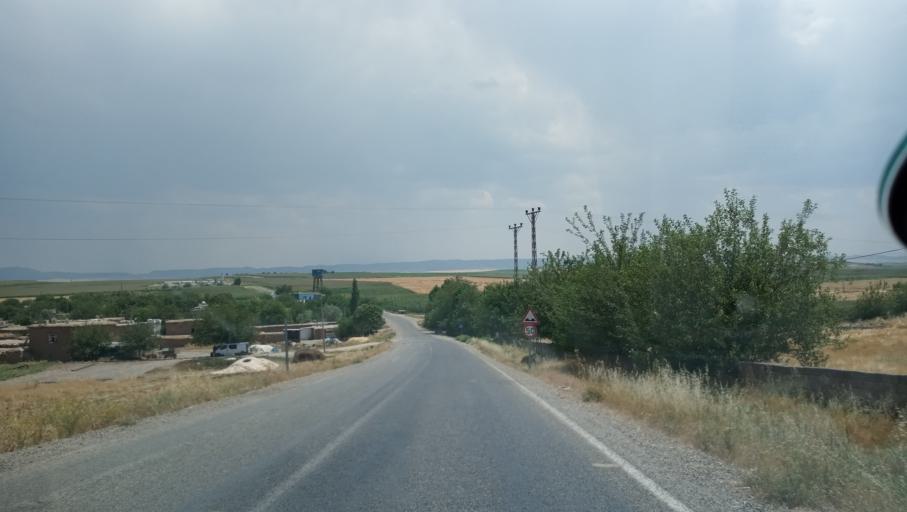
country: TR
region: Diyarbakir
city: Tepe
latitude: 37.7312
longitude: 40.8263
